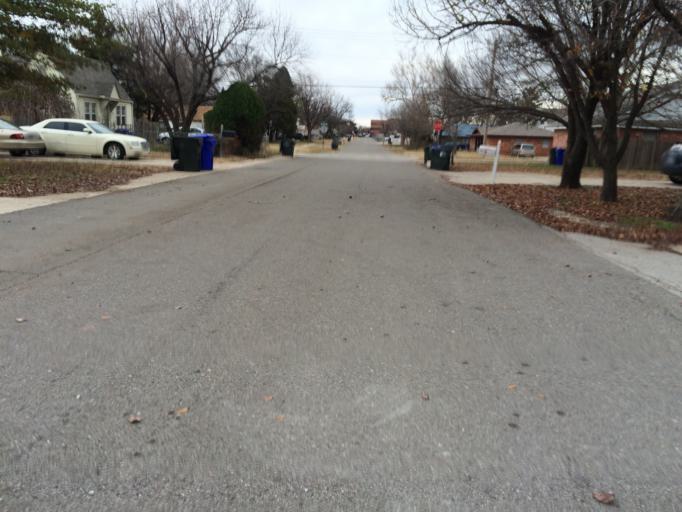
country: US
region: Oklahoma
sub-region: Cleveland County
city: Norman
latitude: 35.2324
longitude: -97.4452
